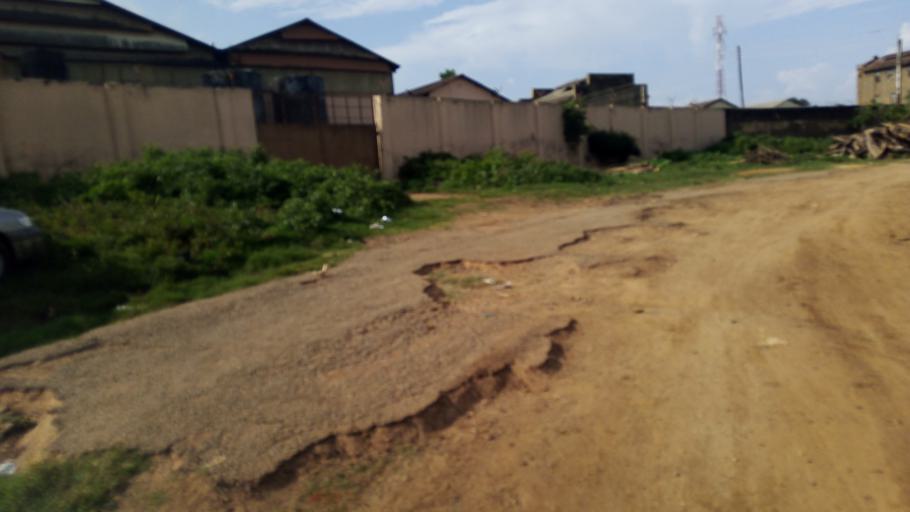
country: UG
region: Eastern Region
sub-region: Mbale District
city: Mbale
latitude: 1.0782
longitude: 34.1622
